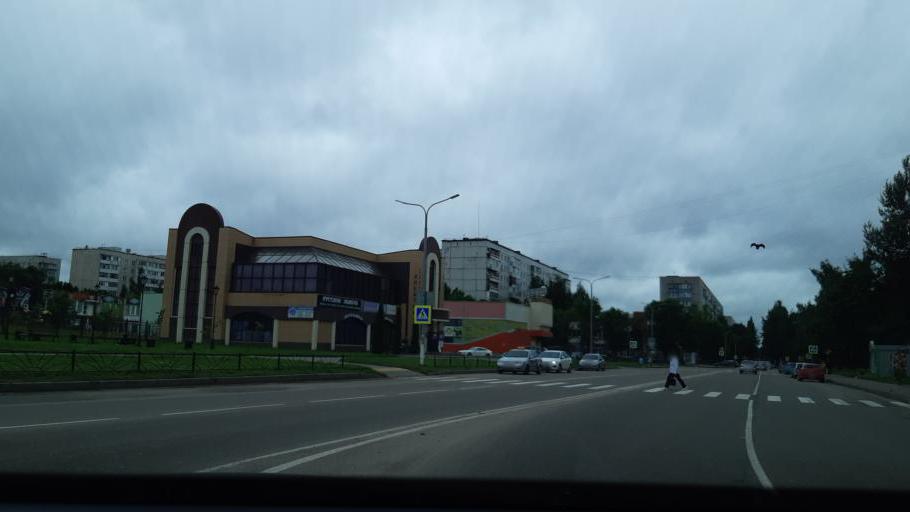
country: RU
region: Smolensk
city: Desnogorsk
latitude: 54.1529
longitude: 33.2879
